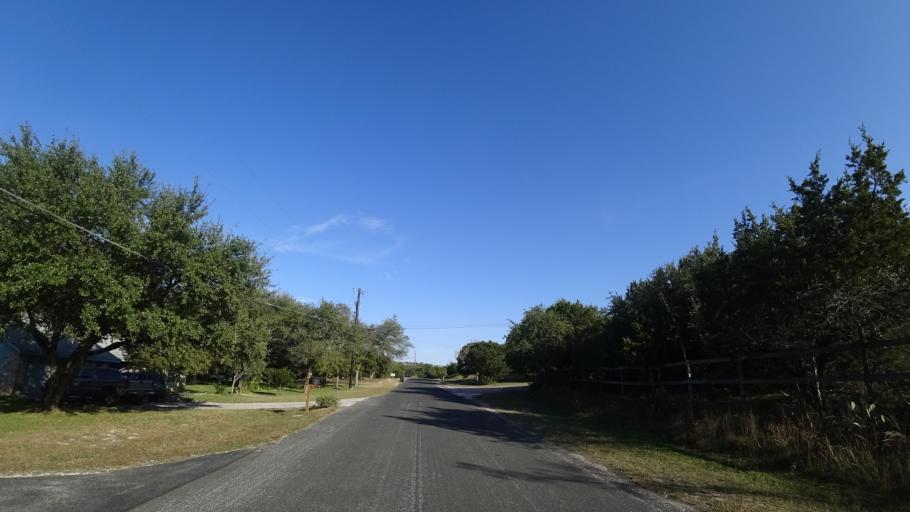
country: US
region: Texas
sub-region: Travis County
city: Barton Creek
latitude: 30.2421
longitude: -97.9099
